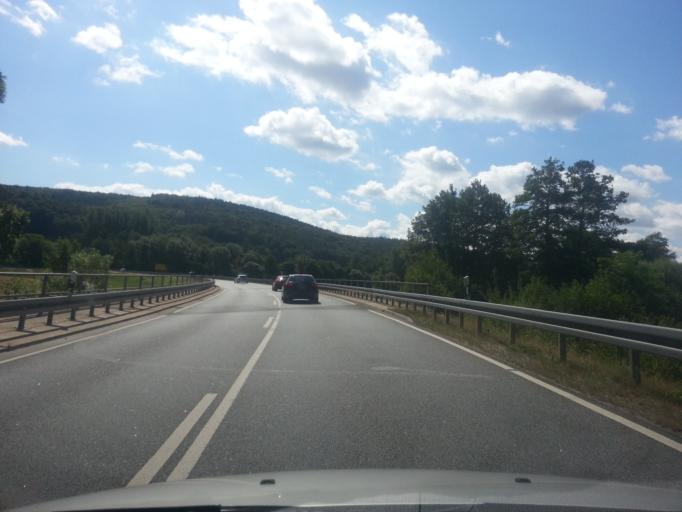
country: DE
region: Hesse
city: Hochst im Odenwald
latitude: 49.7858
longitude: 8.9904
